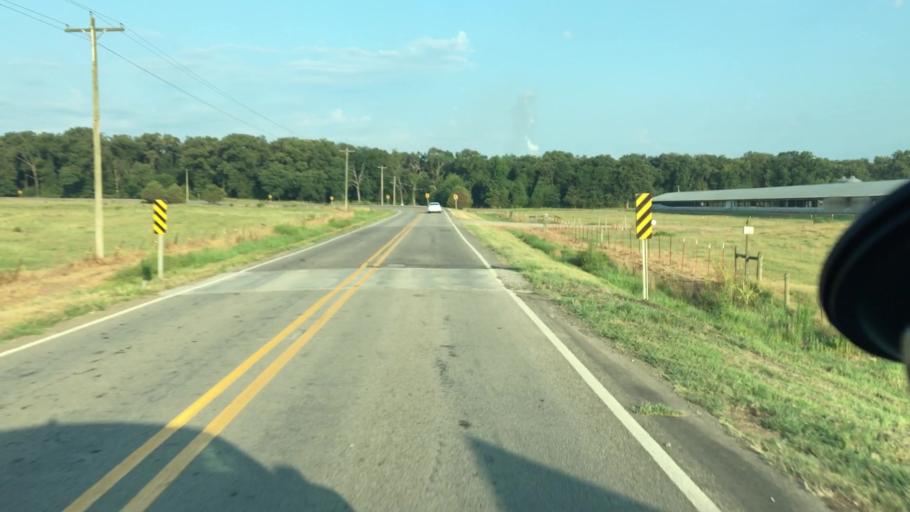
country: US
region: Arkansas
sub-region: Johnson County
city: Coal Hill
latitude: 35.3794
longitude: -93.5578
